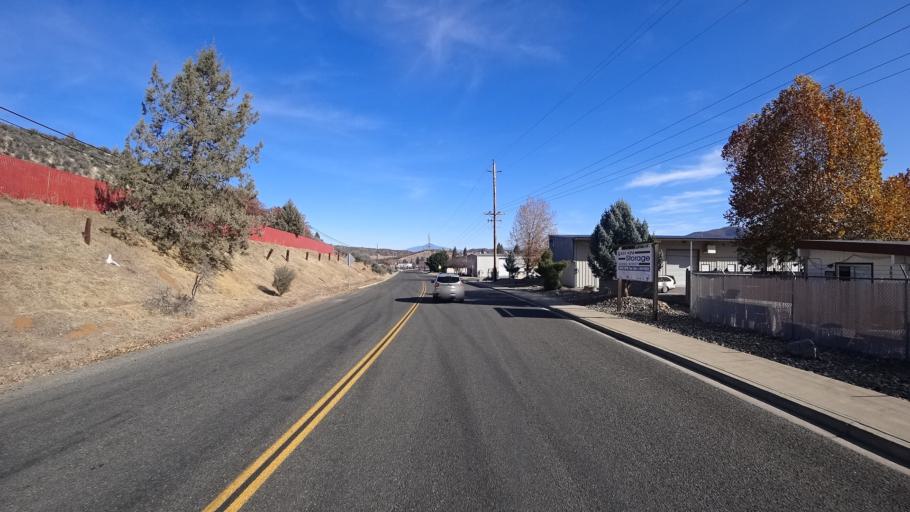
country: US
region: California
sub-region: Siskiyou County
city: Yreka
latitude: 41.7117
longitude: -122.6474
